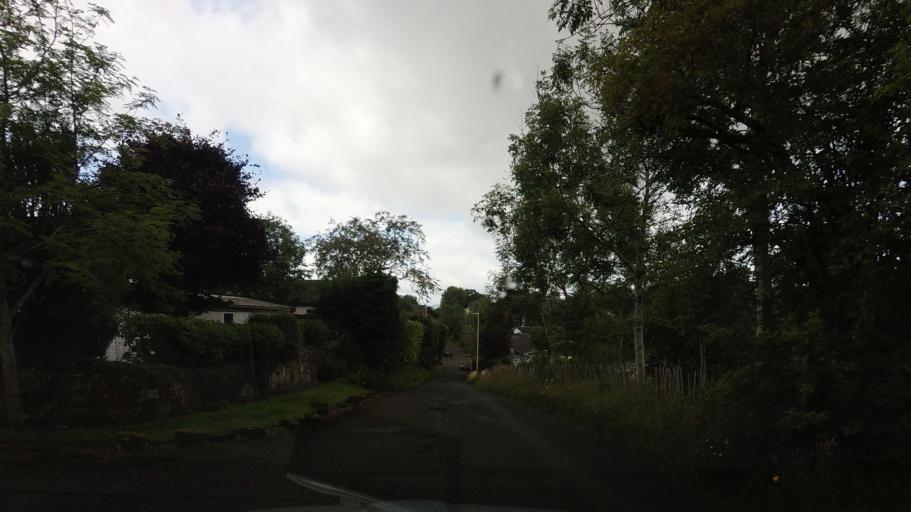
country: GB
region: Scotland
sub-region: Stirling
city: Killearn
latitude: 56.0652
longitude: -4.4495
